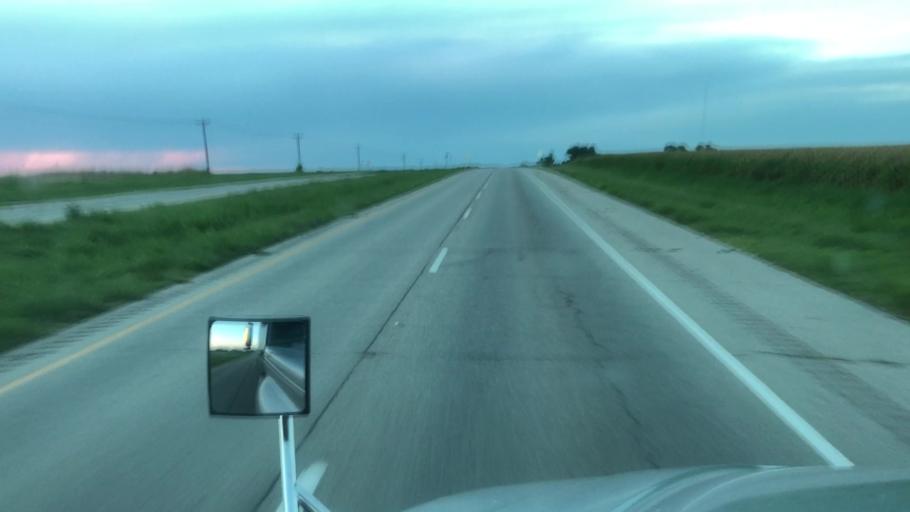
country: US
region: Oklahoma
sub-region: Kay County
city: Newkirk
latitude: 36.8011
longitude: -97.0672
